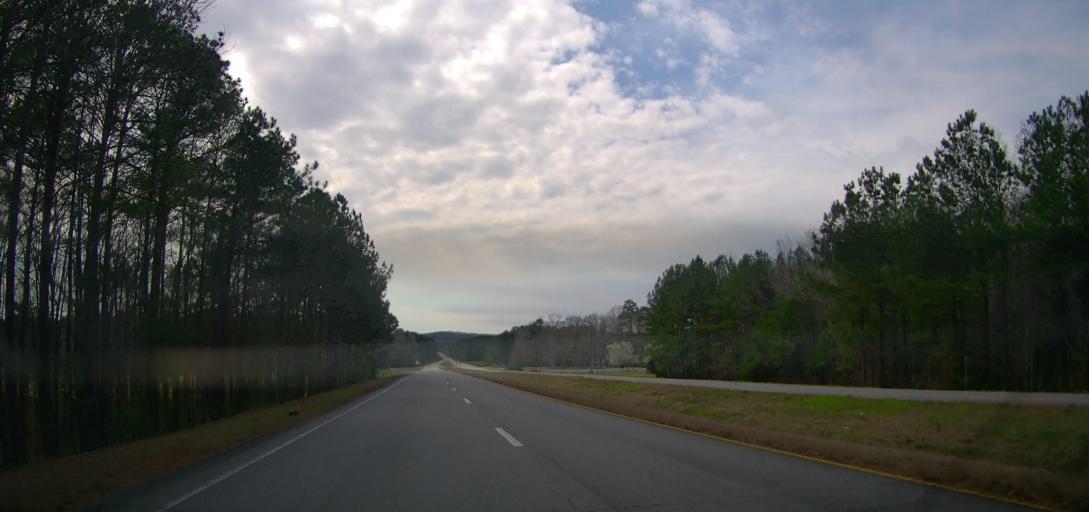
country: US
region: Alabama
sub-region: Marion County
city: Winfield
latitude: 33.9325
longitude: -87.7024
